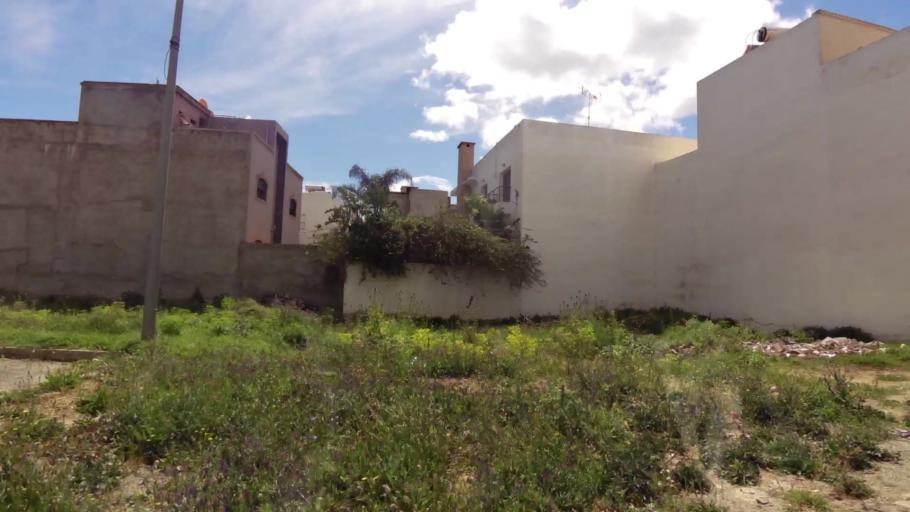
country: MA
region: Tanger-Tetouan
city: Tetouan
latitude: 35.5833
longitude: -5.3346
